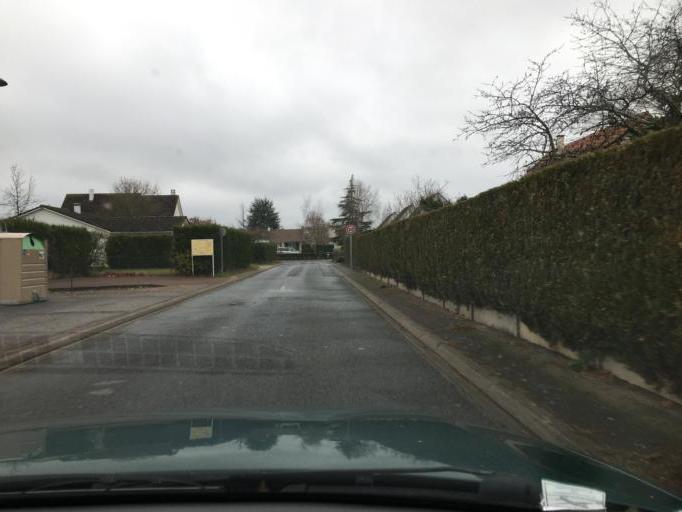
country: FR
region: Centre
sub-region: Departement du Loiret
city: Olivet
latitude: 47.8625
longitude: 1.8901
